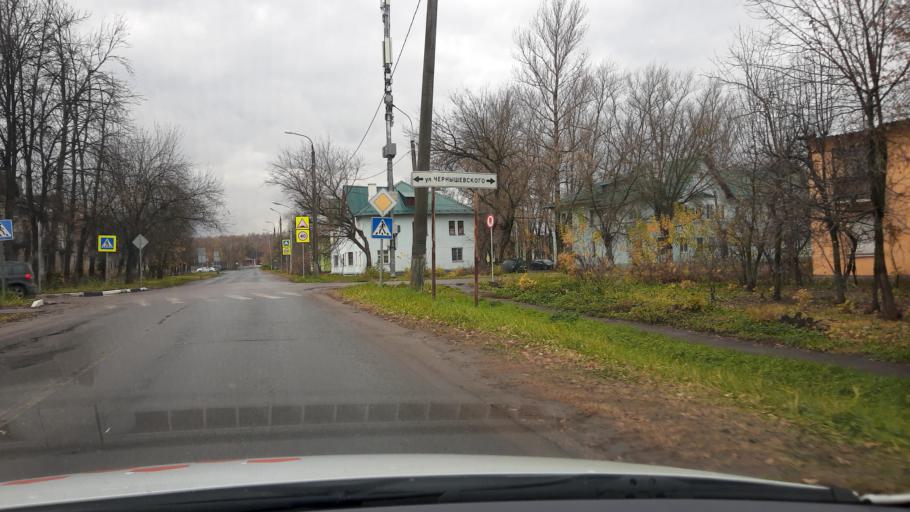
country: RU
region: Moskovskaya
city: Elektrostal'
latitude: 55.7856
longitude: 38.4373
